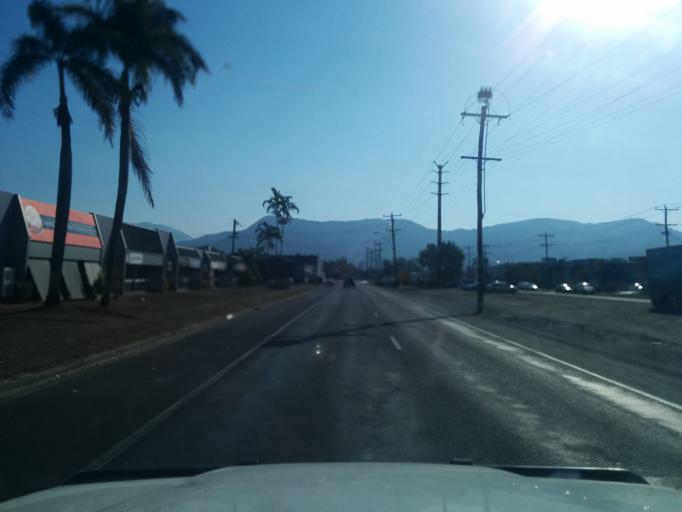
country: AU
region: Queensland
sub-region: Cairns
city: Woree
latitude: -16.9407
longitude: 145.7603
